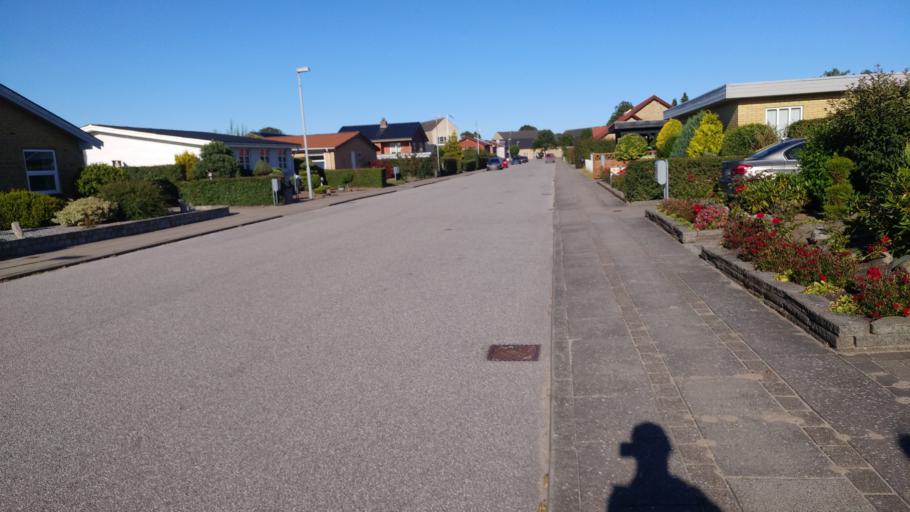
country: DK
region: North Denmark
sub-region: Frederikshavn Kommune
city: Frederikshavn
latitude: 57.4510
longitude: 10.5238
